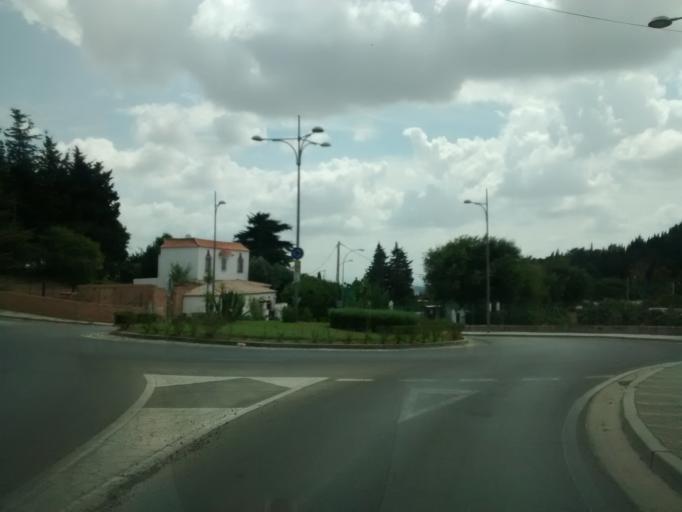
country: ES
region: Andalusia
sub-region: Provincia de Cadiz
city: Medina Sidonia
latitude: 36.4521
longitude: -5.9241
